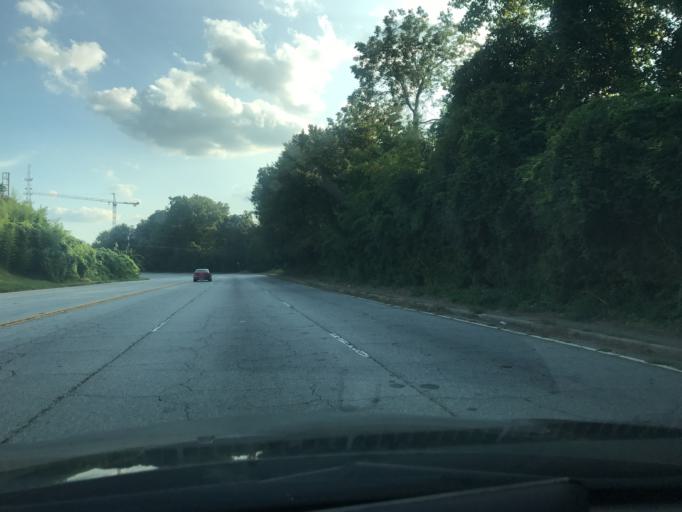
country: US
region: Georgia
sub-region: DeKalb County
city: Avondale Estates
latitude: 33.7790
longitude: -84.2795
